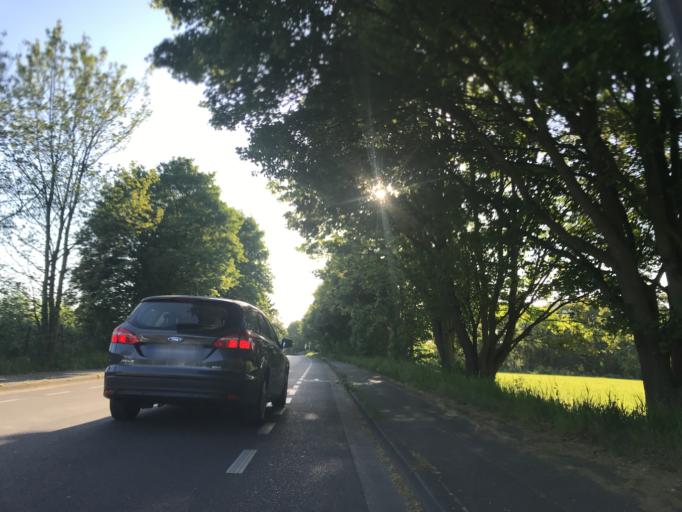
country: DE
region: North Rhine-Westphalia
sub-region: Regierungsbezirk Koln
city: Bonn
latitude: 50.7527
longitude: 7.1363
